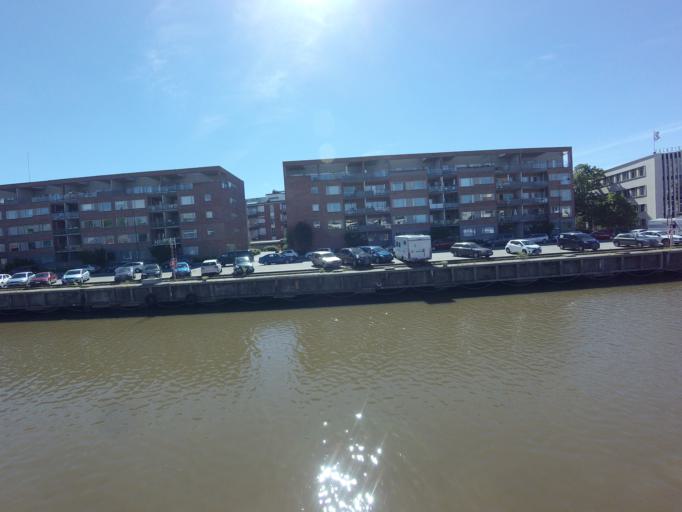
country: FI
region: Varsinais-Suomi
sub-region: Turku
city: Turku
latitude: 60.4388
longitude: 22.2437
